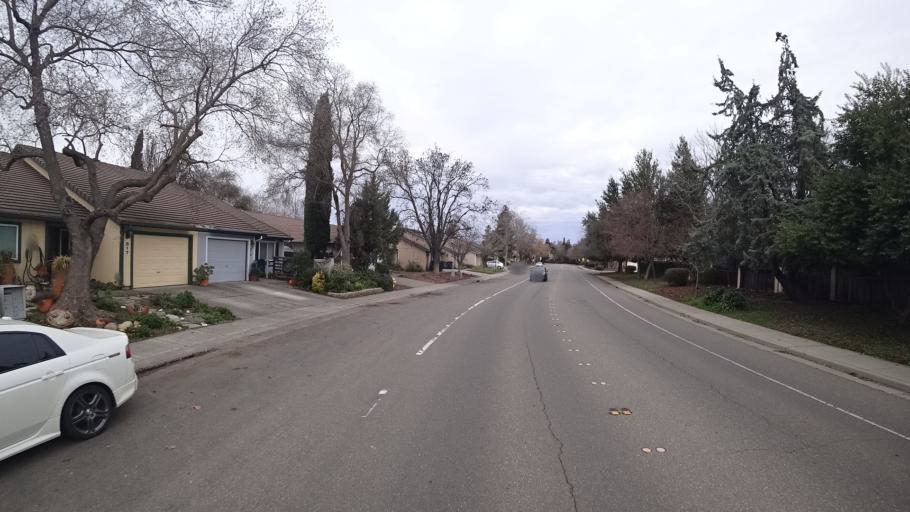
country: US
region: California
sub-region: Yolo County
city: Davis
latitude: 38.5535
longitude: -121.7164
